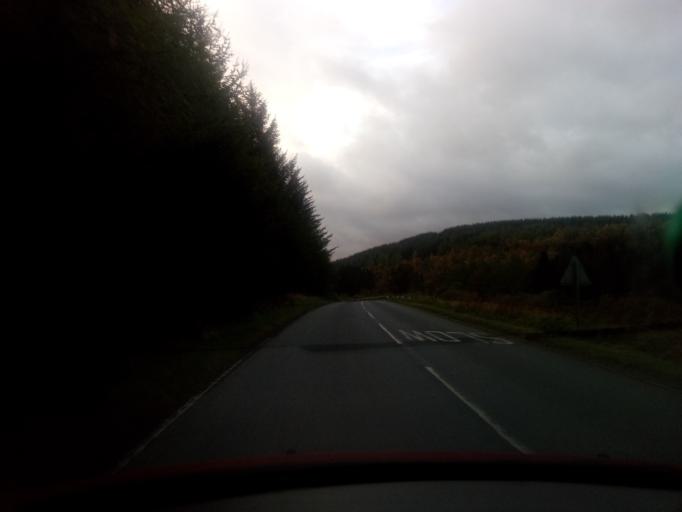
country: GB
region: Scotland
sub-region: The Scottish Borders
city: Hawick
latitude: 55.3633
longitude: -2.6502
